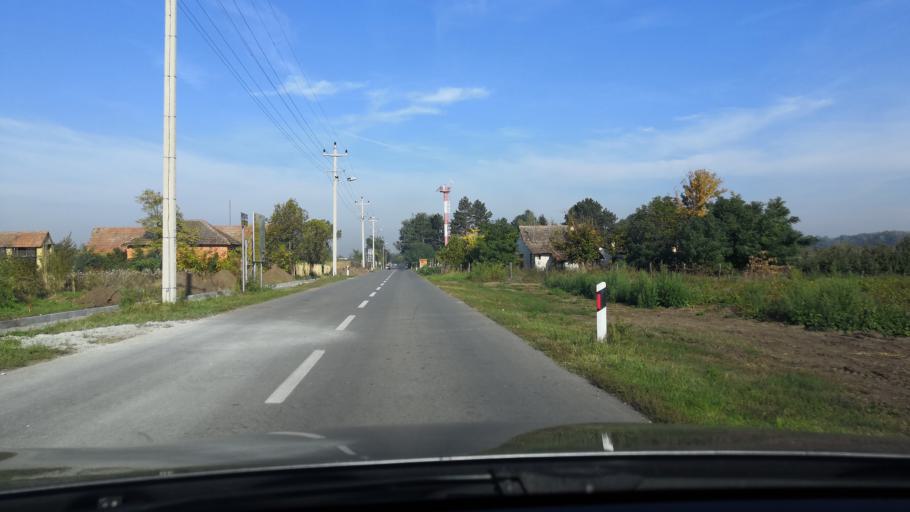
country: HU
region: Csongrad
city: Morahalom
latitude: 46.1393
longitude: 19.8483
